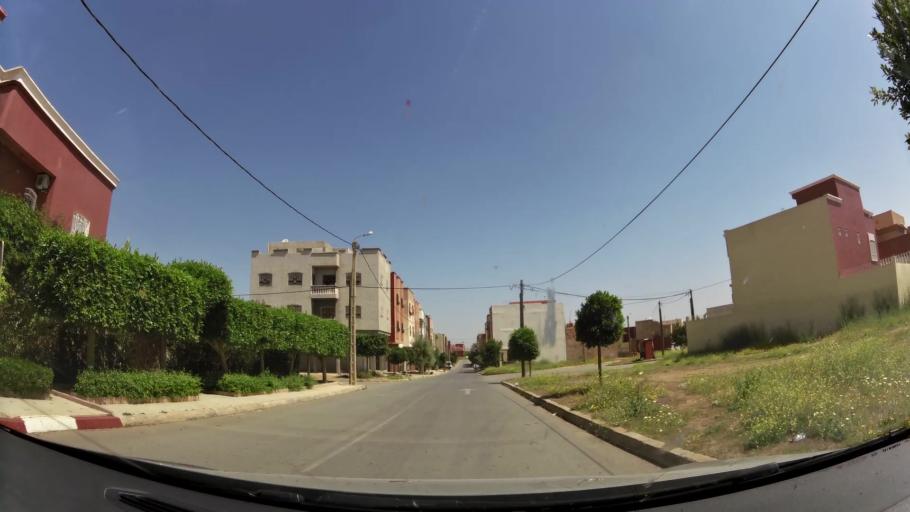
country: MA
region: Rabat-Sale-Zemmour-Zaer
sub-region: Khemisset
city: Khemisset
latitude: 33.8059
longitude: -6.0887
